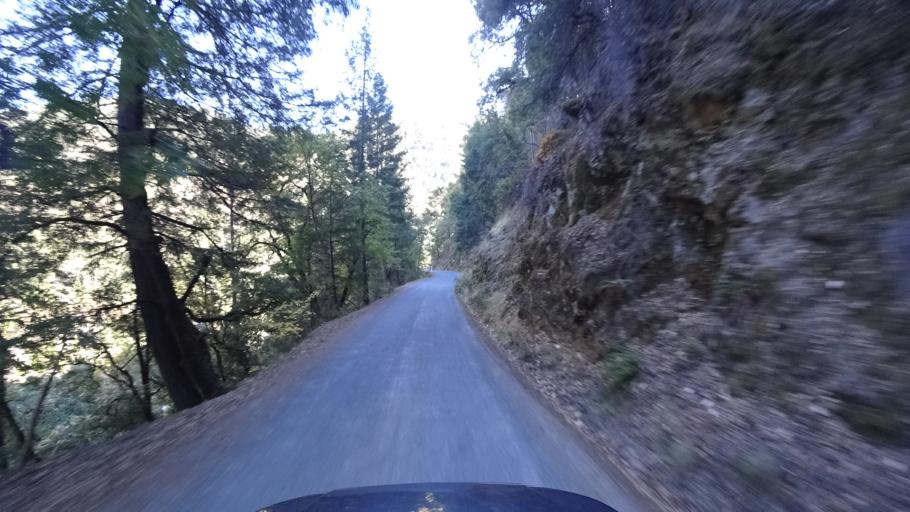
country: US
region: California
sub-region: Humboldt County
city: Willow Creek
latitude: 41.2808
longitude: -123.2650
